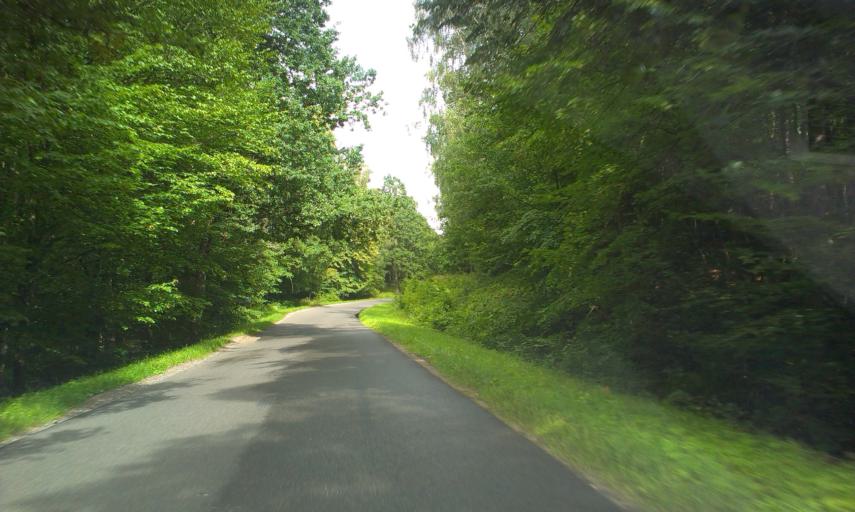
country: PL
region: Greater Poland Voivodeship
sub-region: Powiat zlotowski
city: Okonek
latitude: 53.5339
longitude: 16.8986
